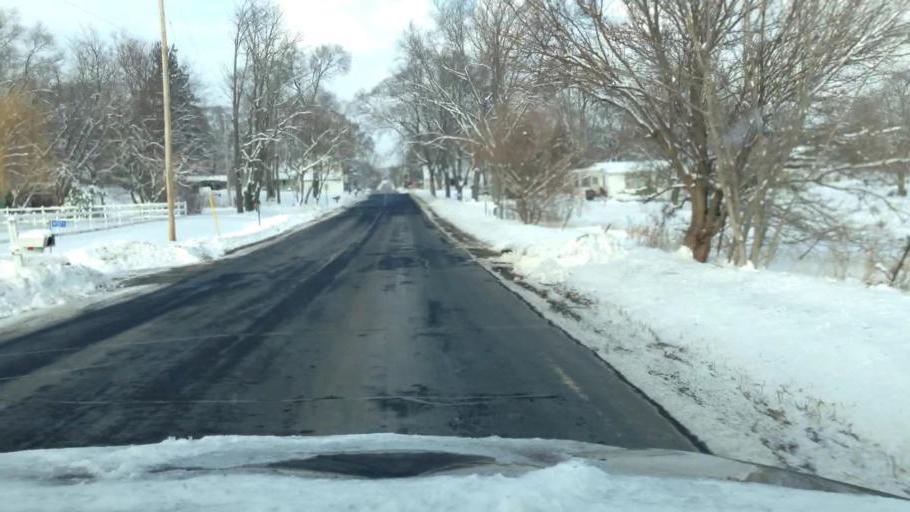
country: US
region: Wisconsin
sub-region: Walworth County
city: East Troy
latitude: 42.7768
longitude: -88.4451
